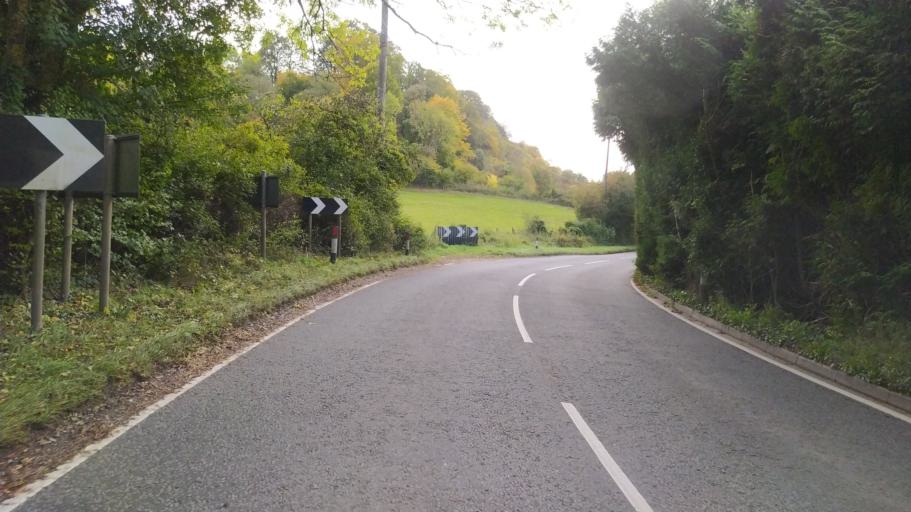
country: GB
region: England
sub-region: Hampshire
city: Romsey
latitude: 51.0490
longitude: -1.5171
